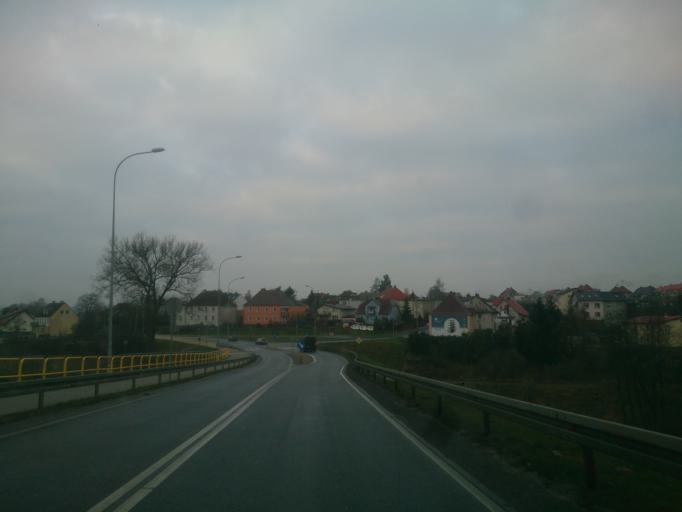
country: PL
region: Pomeranian Voivodeship
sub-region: Powiat bytowski
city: Bytow
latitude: 54.1653
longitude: 17.5053
